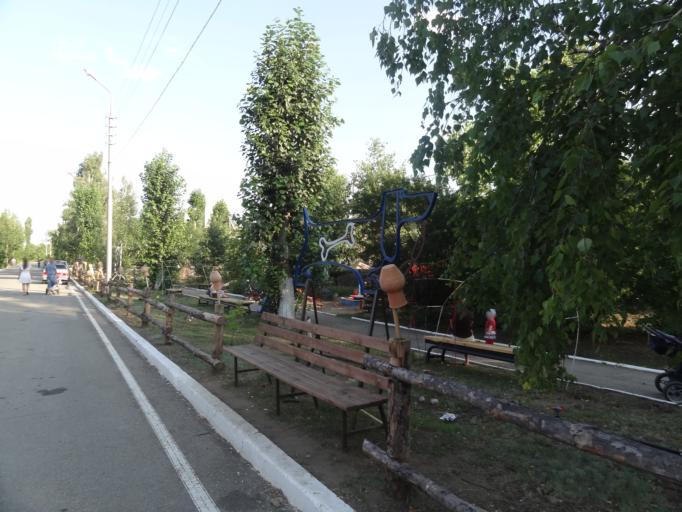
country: RU
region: Saratov
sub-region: Saratovskiy Rayon
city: Saratov
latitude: 51.5421
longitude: 46.0610
